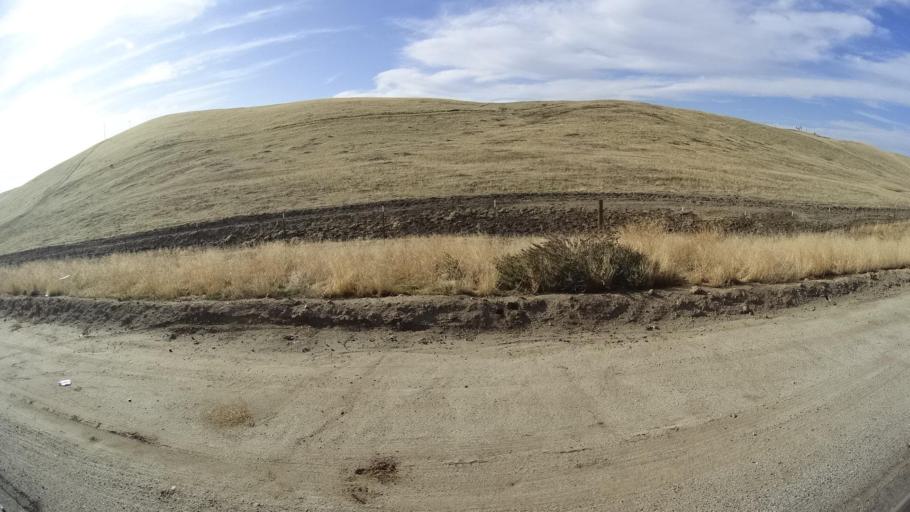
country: US
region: California
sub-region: Kern County
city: Oildale
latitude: 35.6076
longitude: -118.9599
